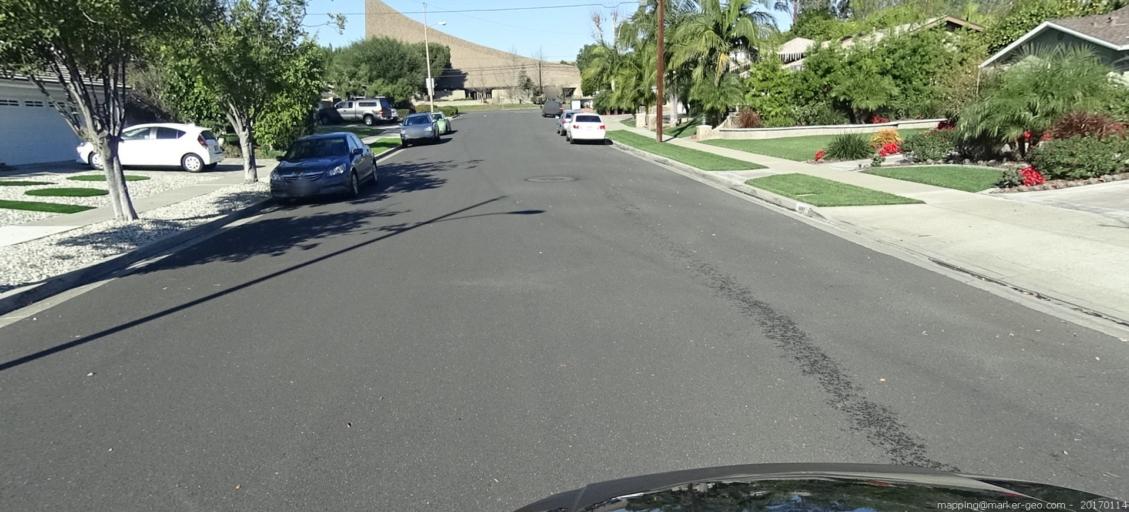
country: US
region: California
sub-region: Orange County
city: Tustin
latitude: 33.7589
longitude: -117.8199
